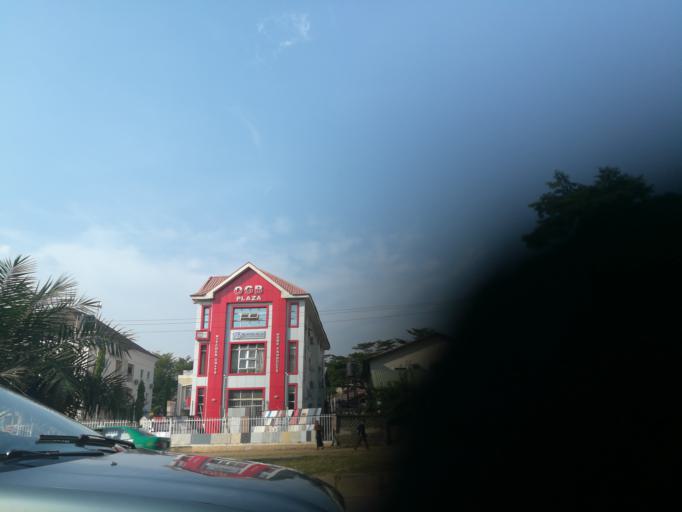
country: NG
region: Abuja Federal Capital Territory
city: Abuja
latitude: 9.0676
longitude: 7.4489
